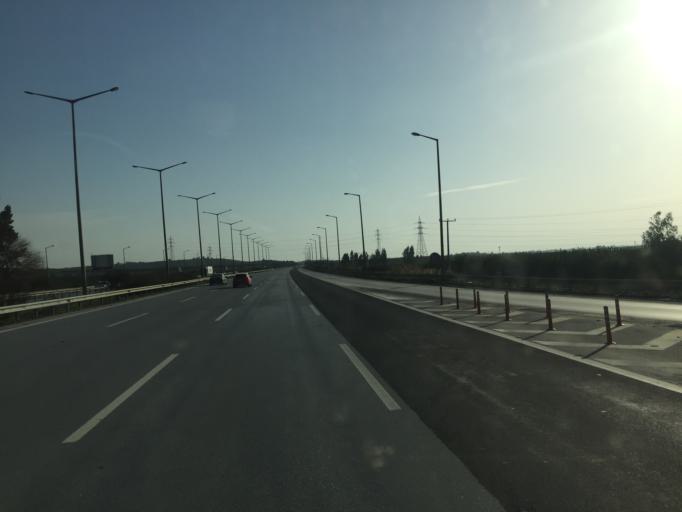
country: TR
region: Mersin
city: Yenice
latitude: 37.0235
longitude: 35.0646
